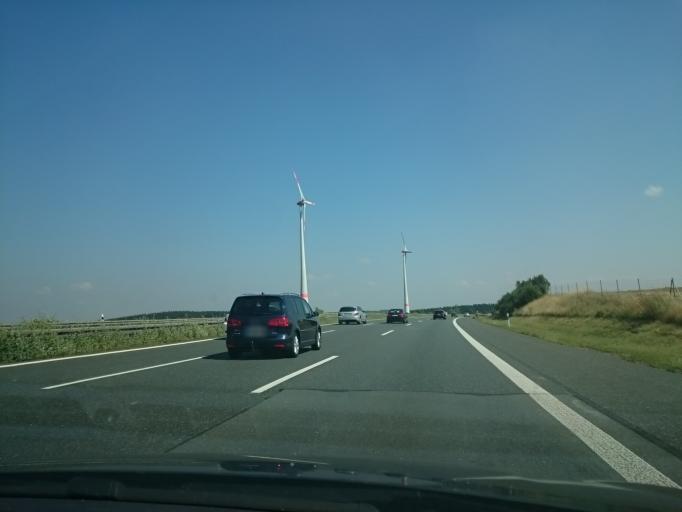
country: DE
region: Bavaria
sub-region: Upper Franconia
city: Munchberg
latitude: 50.2406
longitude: 11.7799
